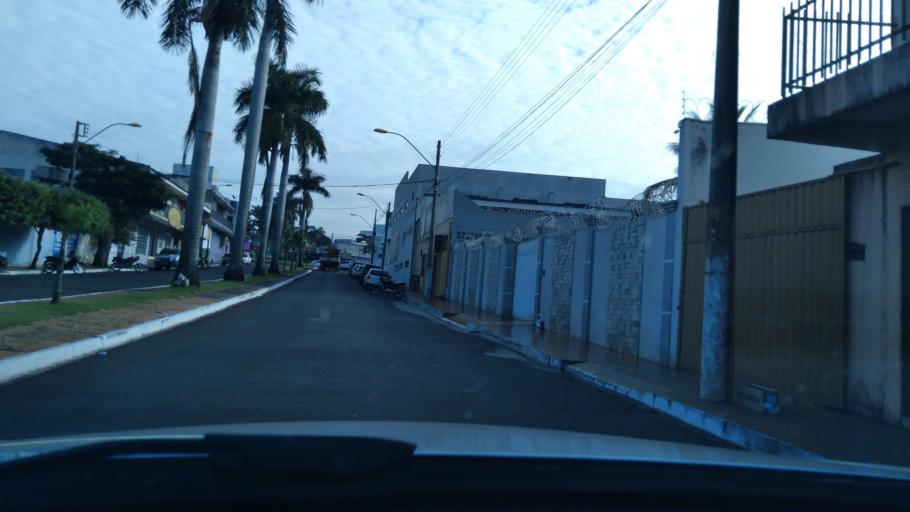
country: BR
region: Goias
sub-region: Mineiros
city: Mineiros
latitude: -17.5643
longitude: -52.5521
